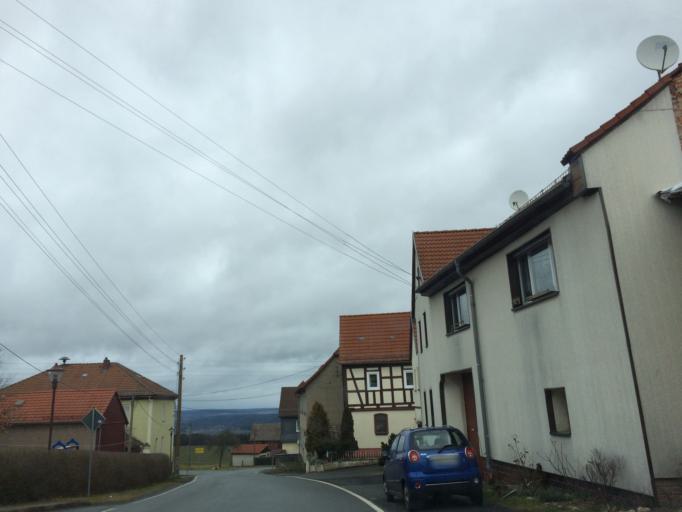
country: DE
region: Thuringia
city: Grobengereuth
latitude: 50.6705
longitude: 11.6819
